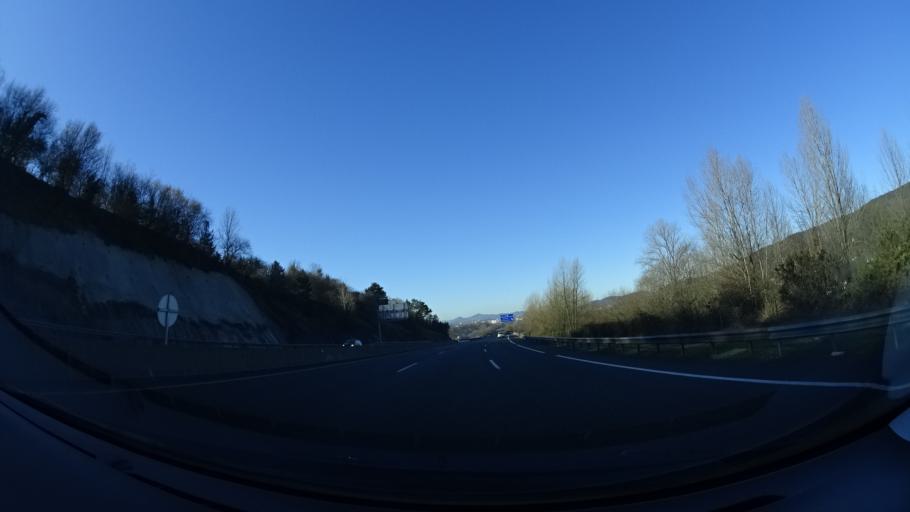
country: ES
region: Basque Country
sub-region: Provincia de Guipuzcoa
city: Lezo
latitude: 43.3156
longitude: -1.8616
